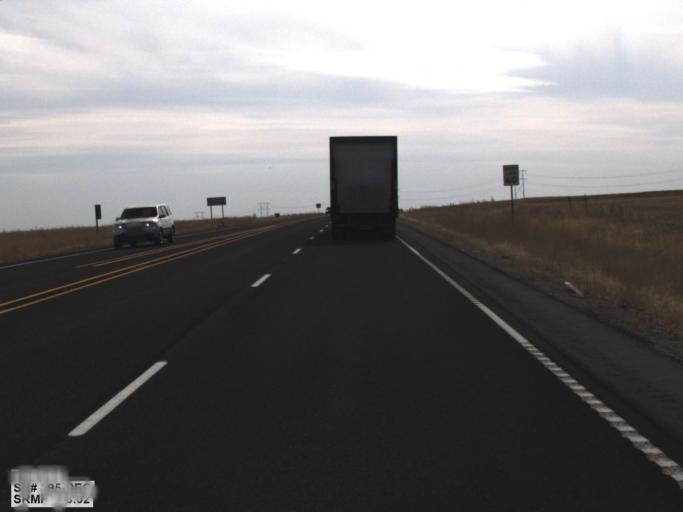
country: US
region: Washington
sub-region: Spokane County
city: Fairwood
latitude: 47.8592
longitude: -117.4219
